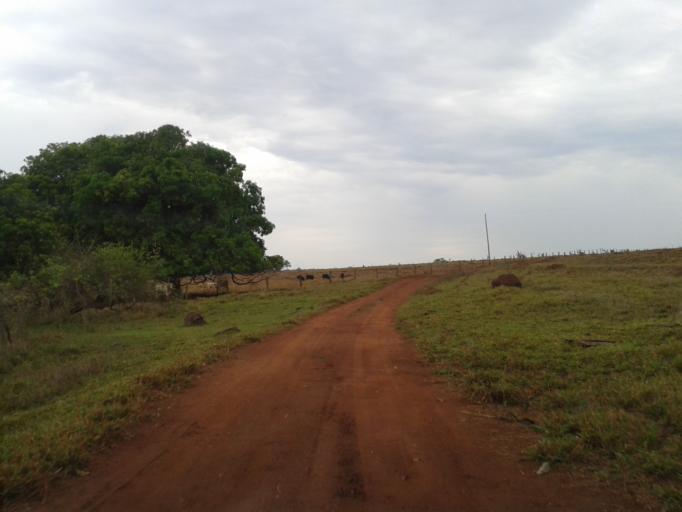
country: BR
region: Minas Gerais
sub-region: Santa Vitoria
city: Santa Vitoria
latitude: -18.8642
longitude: -49.8250
